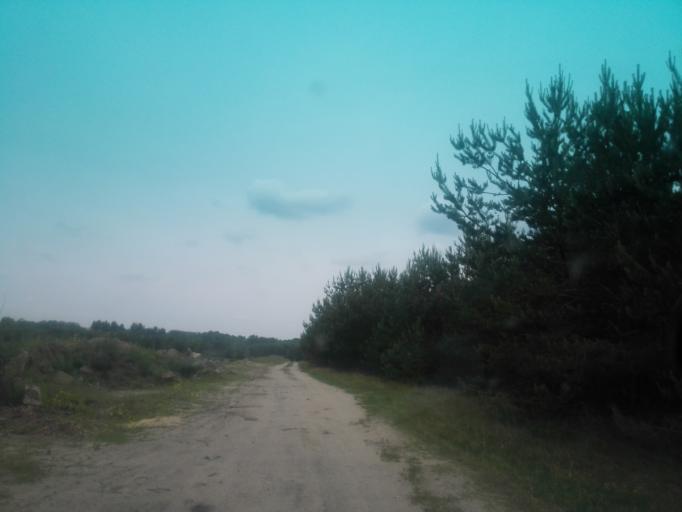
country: PL
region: Silesian Voivodeship
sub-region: Powiat czestochowski
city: Mstow
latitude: 50.8292
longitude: 19.3271
